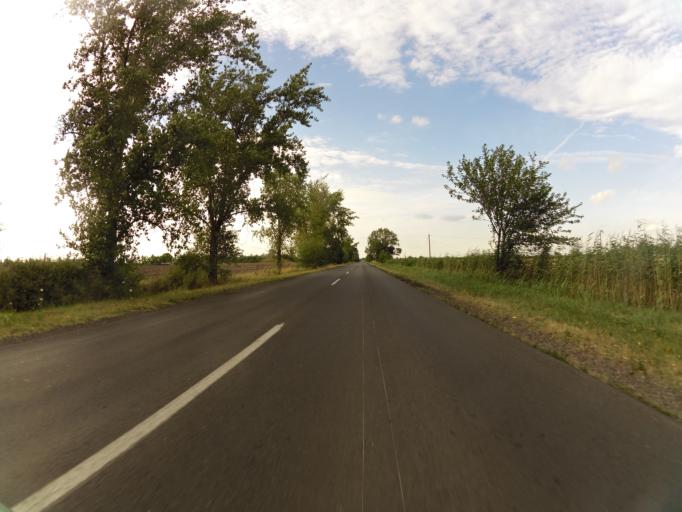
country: HU
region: Csongrad
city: Sandorfalva
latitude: 46.3308
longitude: 20.1333
